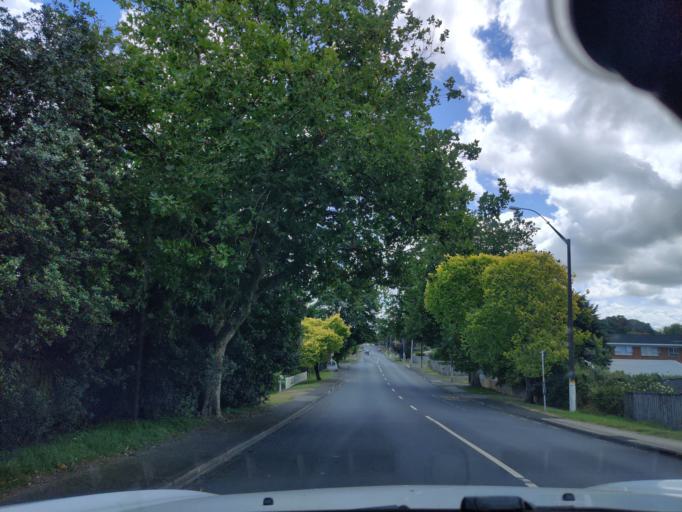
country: NZ
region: Auckland
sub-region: Auckland
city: Papakura
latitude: -37.0688
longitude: 174.9486
